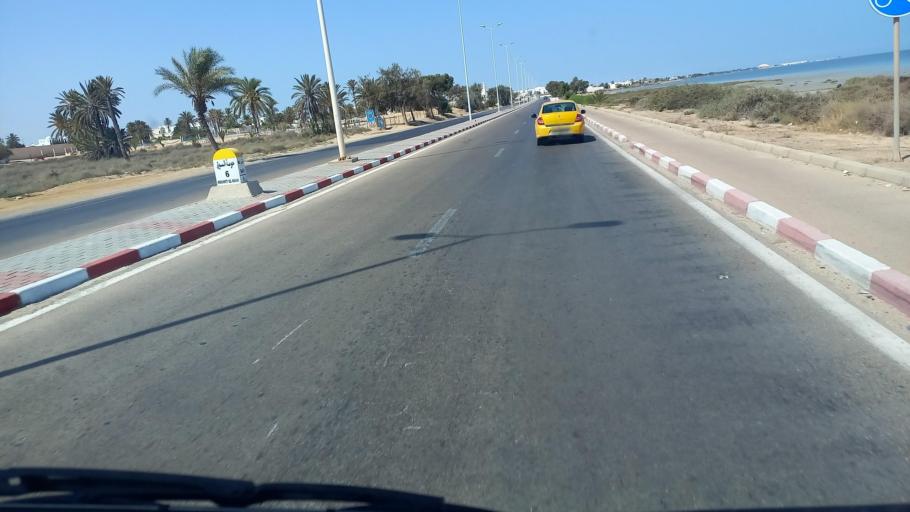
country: TN
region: Madanin
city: Houmt Souk
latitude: 33.8734
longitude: 10.9160
